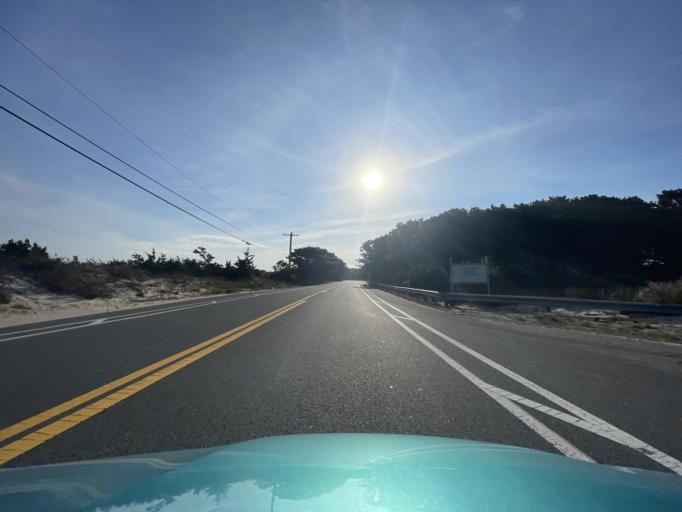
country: US
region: Massachusetts
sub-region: Bristol County
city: Head of Westport
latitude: 41.5087
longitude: -71.0546
